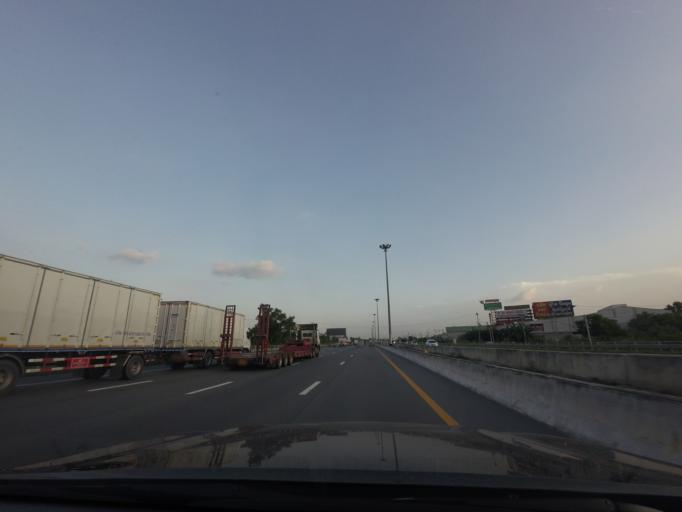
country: TH
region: Pathum Thani
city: Khlong Luang
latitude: 14.0935
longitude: 100.6908
